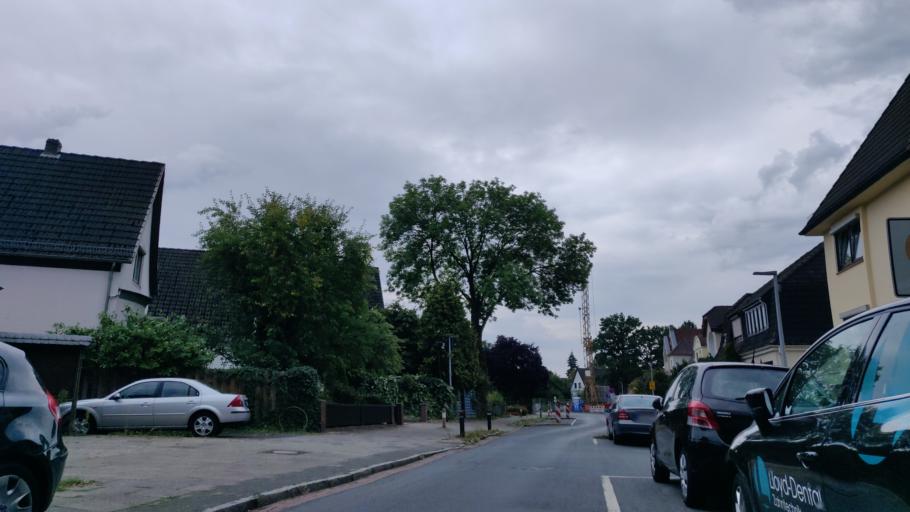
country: DE
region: Lower Saxony
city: Lilienthal
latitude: 53.0980
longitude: 8.8932
